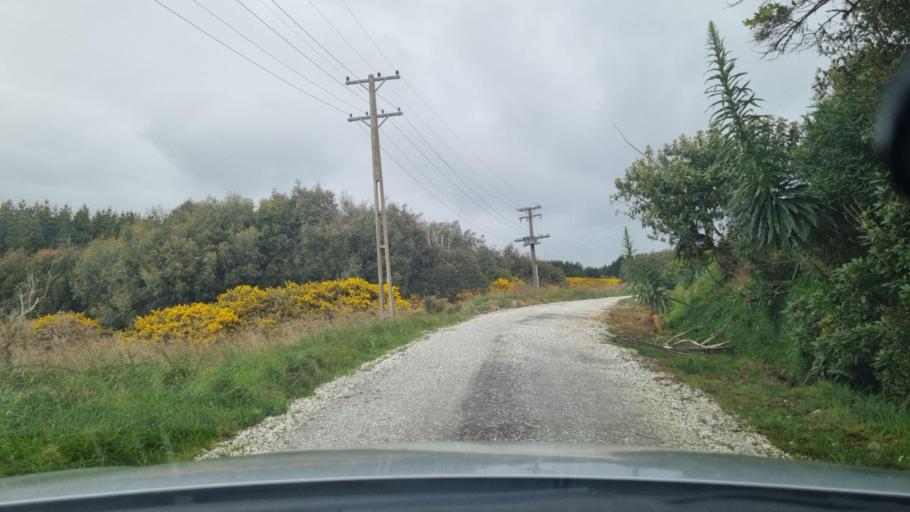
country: NZ
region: Southland
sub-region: Invercargill City
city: Bluff
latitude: -46.5766
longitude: 168.2980
